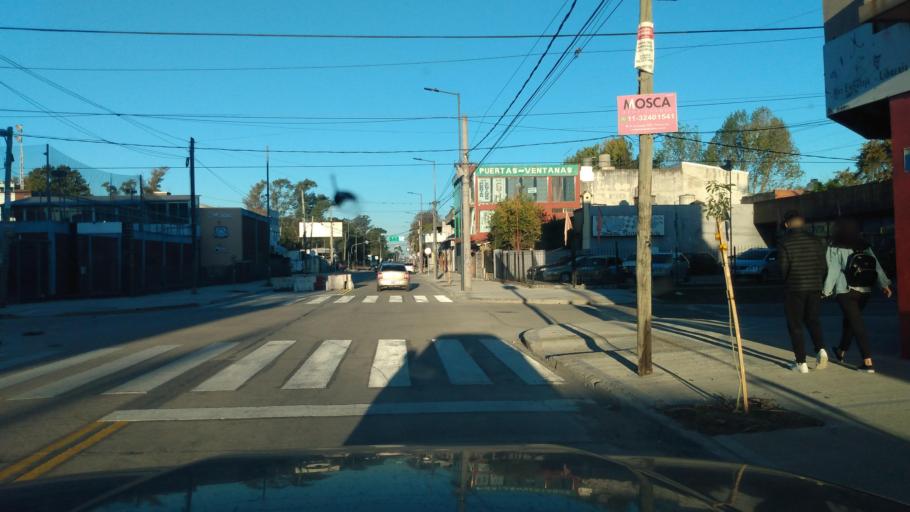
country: AR
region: Buenos Aires
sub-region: Partido de Merlo
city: Merlo
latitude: -34.6516
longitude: -58.7806
